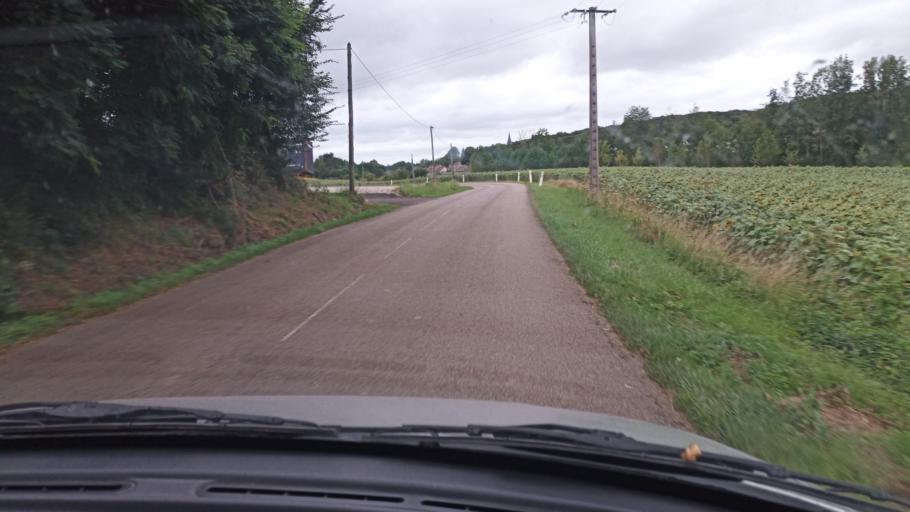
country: FR
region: Bourgogne
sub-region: Departement de l'Yonne
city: Cheroy
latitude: 48.2359
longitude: 3.0547
